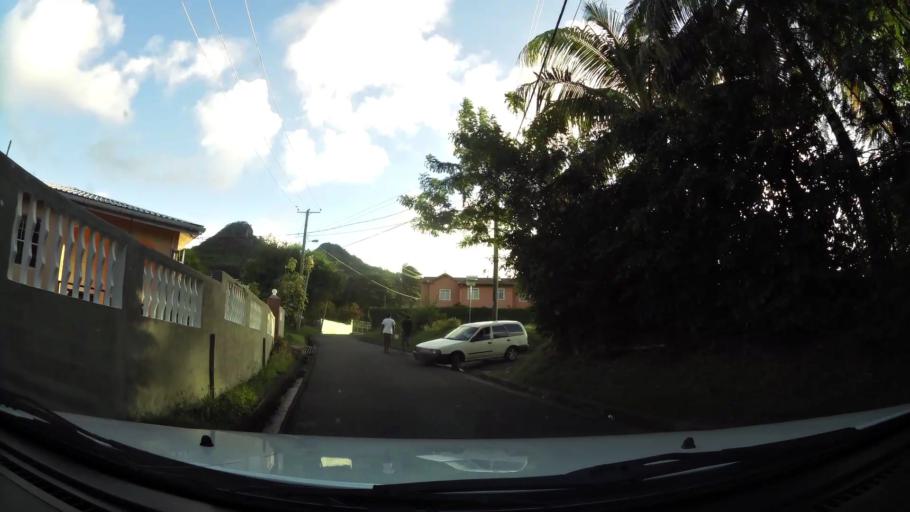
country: LC
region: Gros-Islet
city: Gros Islet
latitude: 14.0618
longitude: -60.9415
